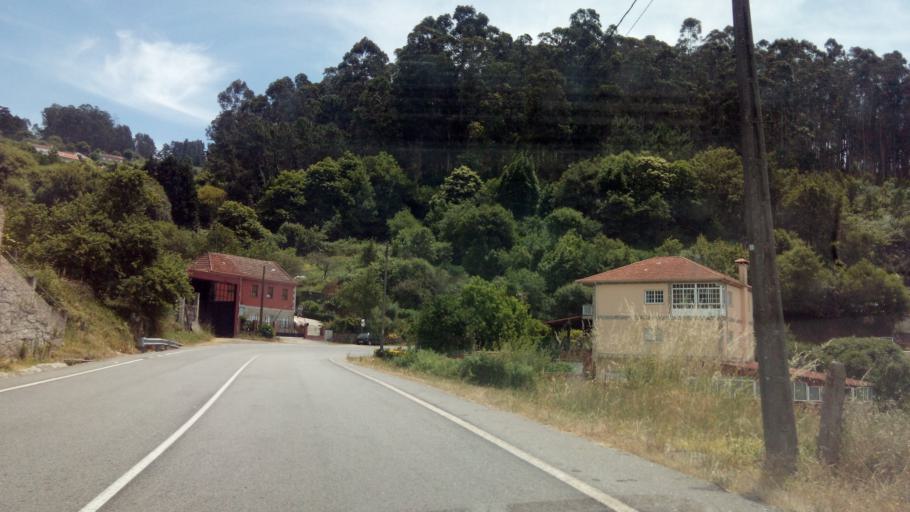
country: ES
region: Galicia
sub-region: Provincia de Pontevedra
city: Marin
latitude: 42.3539
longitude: -8.6959
